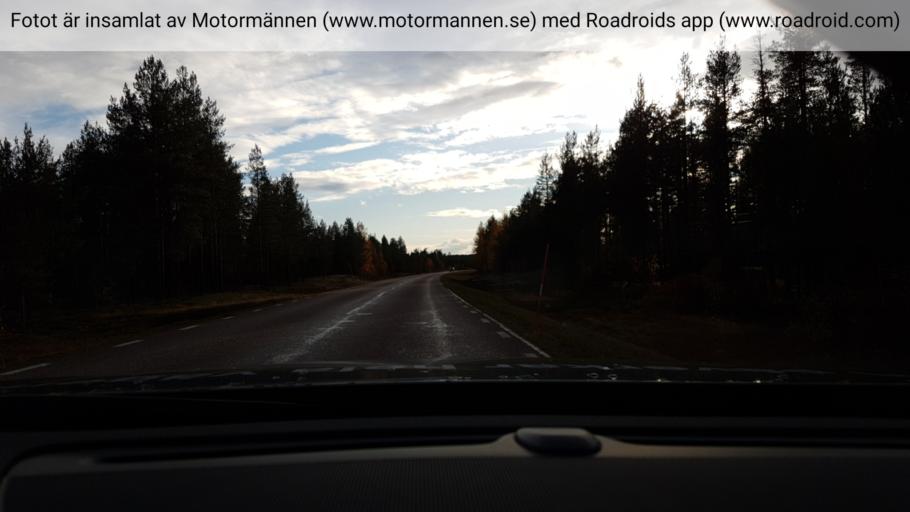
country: SE
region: Norrbotten
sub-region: Pajala Kommun
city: Pajala
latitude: 67.1762
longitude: 22.6944
